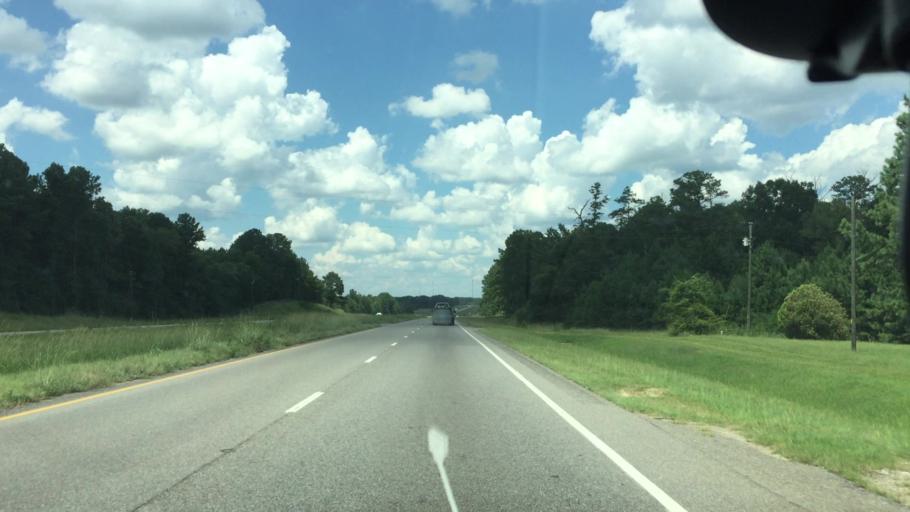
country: US
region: Alabama
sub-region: Montgomery County
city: Taylor
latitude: 32.0176
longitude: -86.0306
